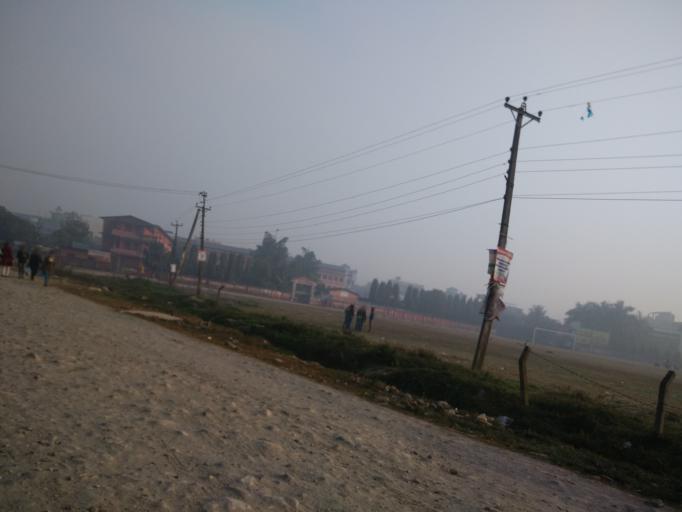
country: NP
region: Central Region
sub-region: Narayani Zone
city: Bharatpur
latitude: 27.6958
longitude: 84.4260
